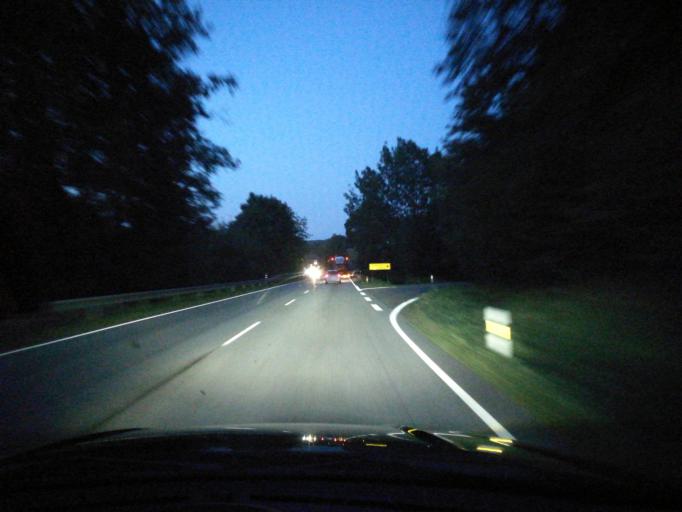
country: DE
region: Bavaria
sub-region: Lower Bavaria
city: Bad Abbach
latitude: 48.9555
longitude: 12.0452
